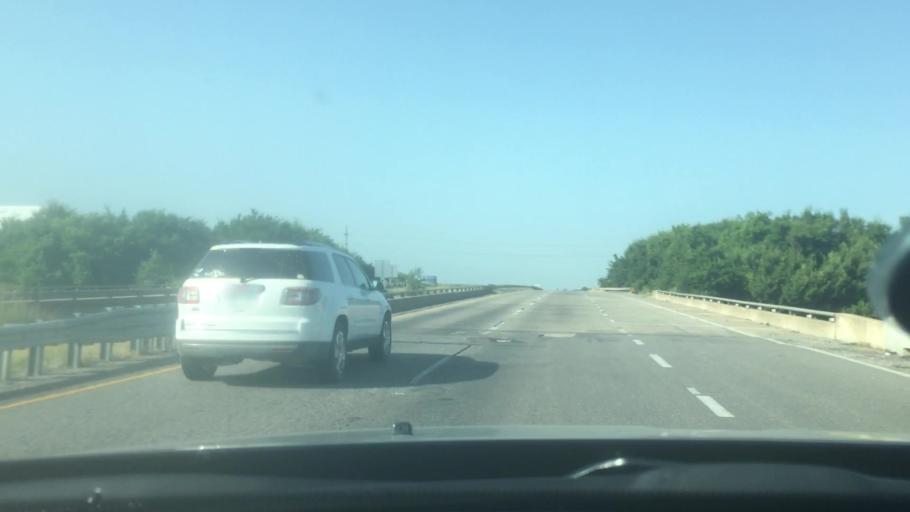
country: US
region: Oklahoma
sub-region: Bryan County
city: Durant
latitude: 33.9984
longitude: -96.4043
